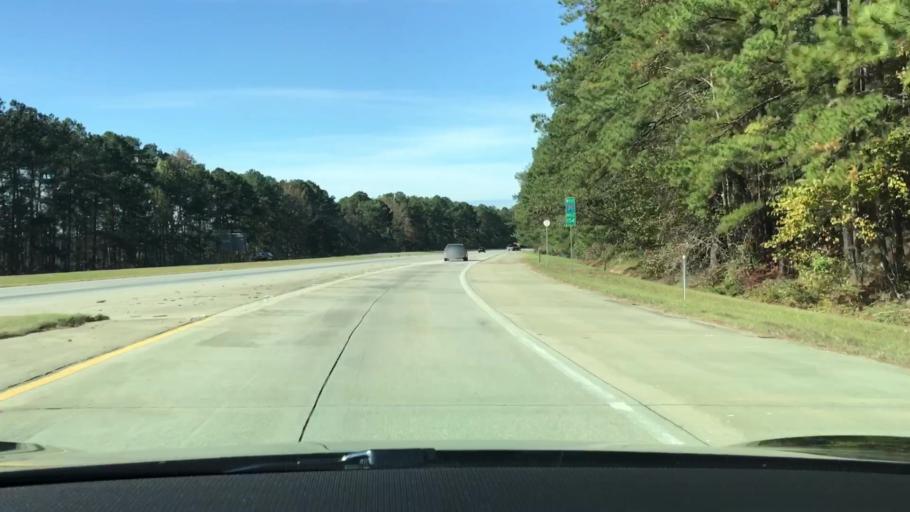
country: US
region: Georgia
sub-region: Taliaferro County
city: Crawfordville
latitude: 33.4985
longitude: -82.8092
